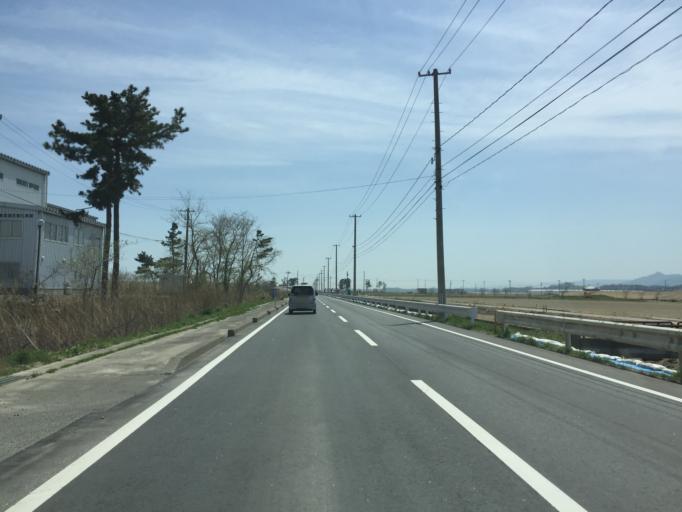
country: JP
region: Miyagi
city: Watari
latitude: 37.9632
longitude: 140.9083
